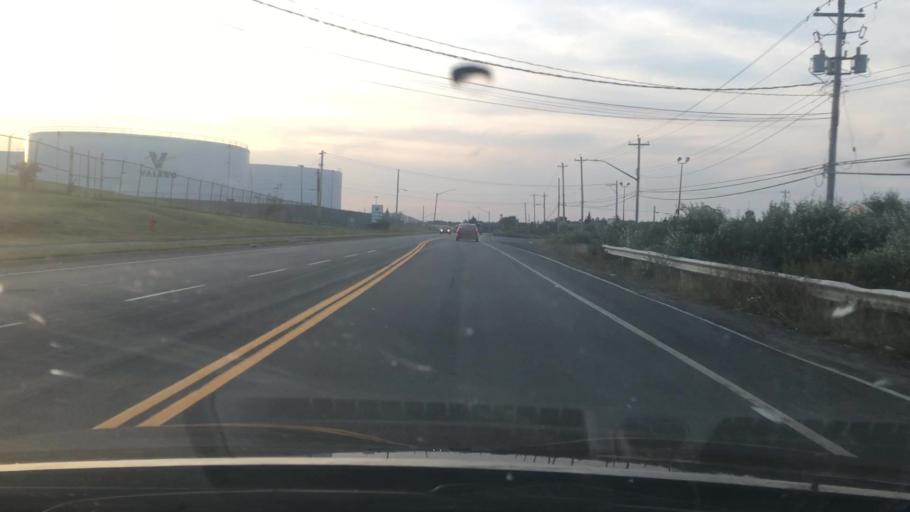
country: CA
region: Nova Scotia
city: Cole Harbour
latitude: 44.6177
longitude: -63.5013
